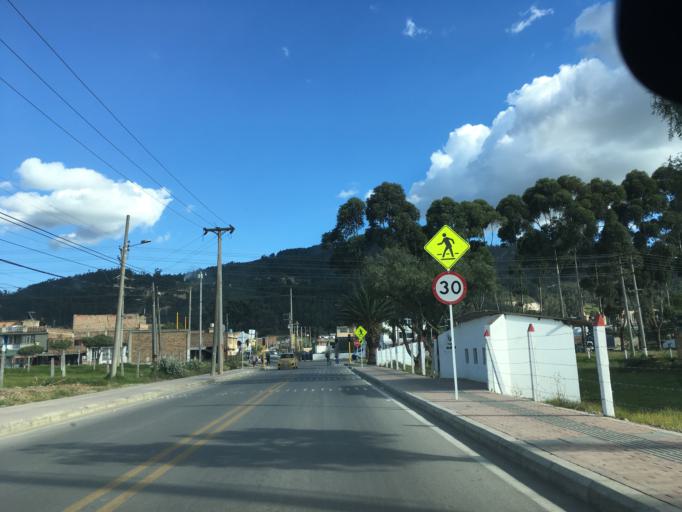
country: CO
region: Boyaca
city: Sogamoso
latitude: 5.7359
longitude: -72.9191
